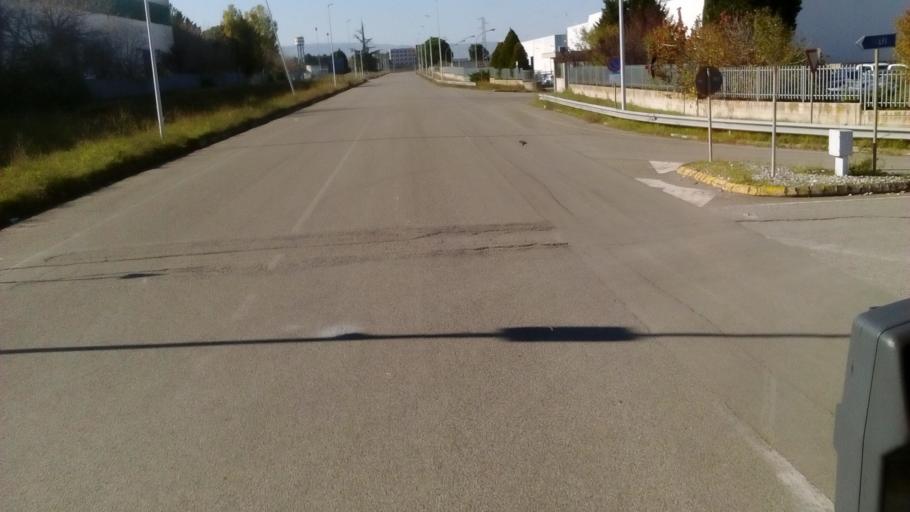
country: IT
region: Basilicate
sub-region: Provincia di Potenza
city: Melfi
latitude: 41.0760
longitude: 15.6828
